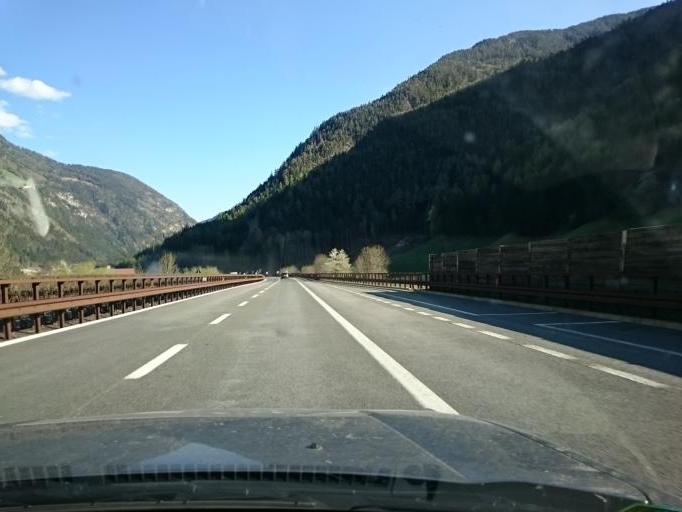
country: IT
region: Trentino-Alto Adige
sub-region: Bolzano
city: Campo di Trens
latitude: 46.8495
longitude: 11.5144
